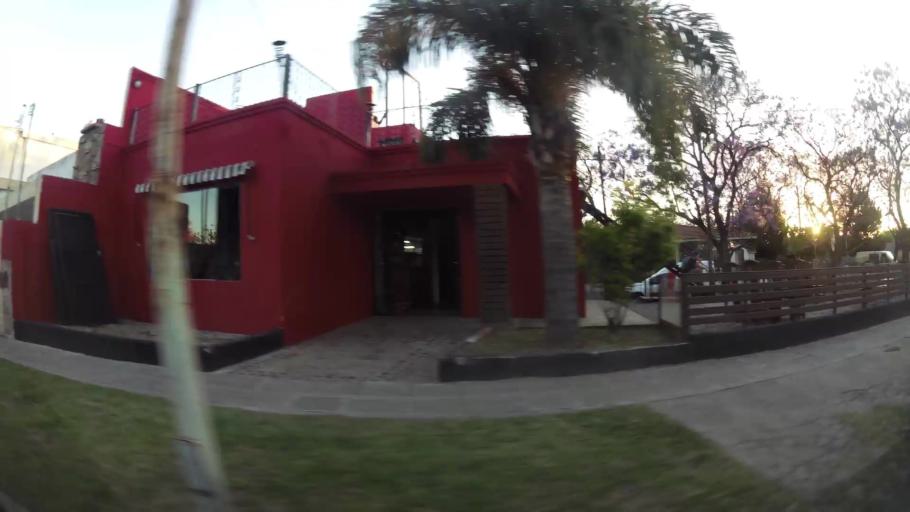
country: AR
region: Cordoba
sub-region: Departamento de Capital
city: Cordoba
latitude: -31.3721
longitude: -64.2215
